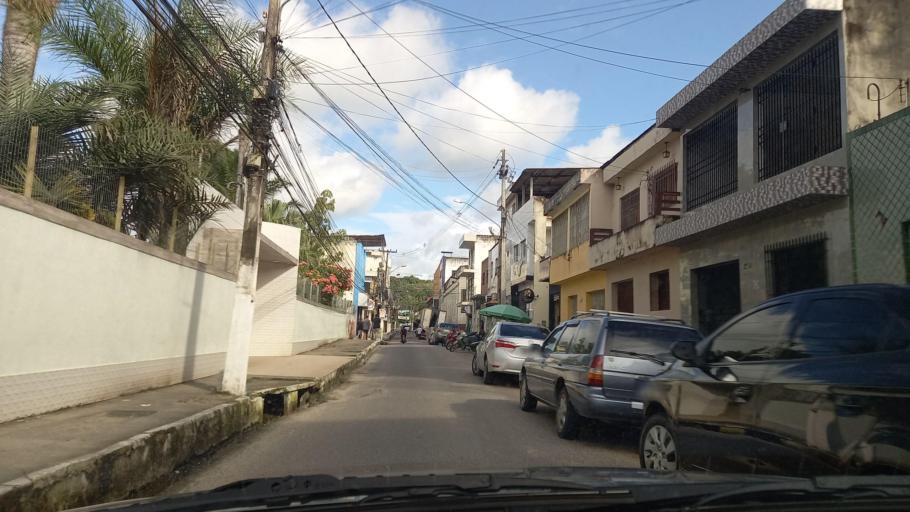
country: BR
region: Pernambuco
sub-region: Palmares
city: Palmares
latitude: -8.6838
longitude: -35.5907
